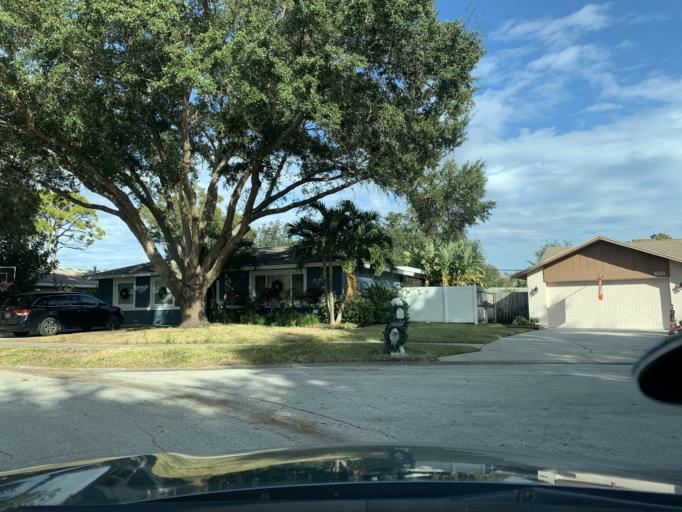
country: US
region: Florida
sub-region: Pinellas County
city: Kenneth City
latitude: 27.8274
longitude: -82.7461
